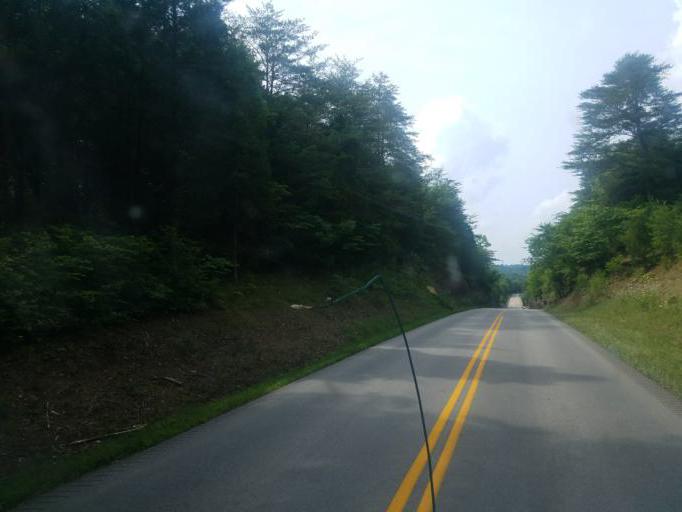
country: US
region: Kentucky
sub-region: Edmonson County
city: Brownsville
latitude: 37.3355
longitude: -86.1259
